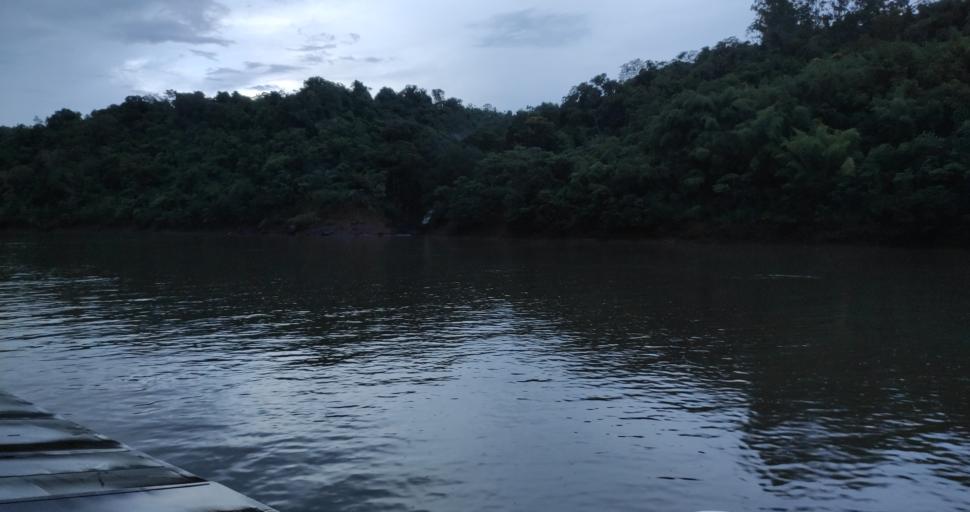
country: AR
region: Misiones
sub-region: Departamento de Iguazu
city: Puerto Iguazu
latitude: -25.5884
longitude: -54.5528
